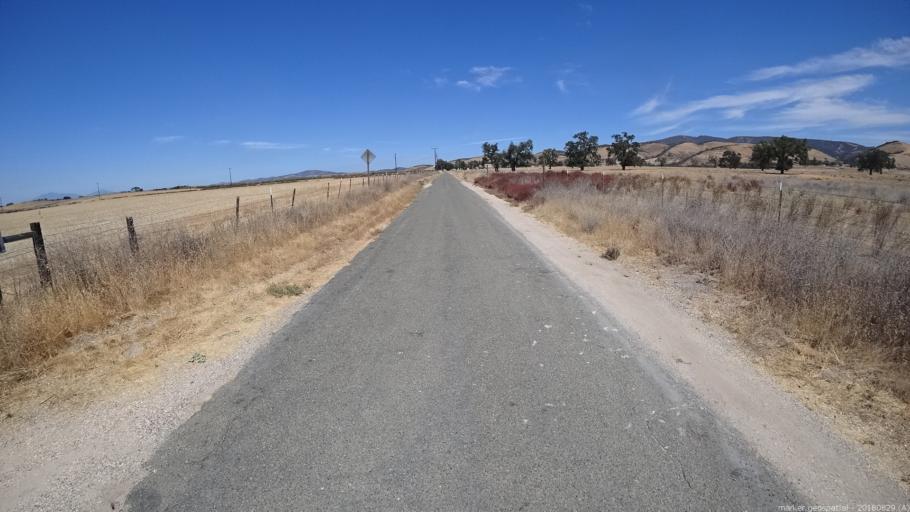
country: US
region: California
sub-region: San Luis Obispo County
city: Lake Nacimiento
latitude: 35.9098
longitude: -121.0380
